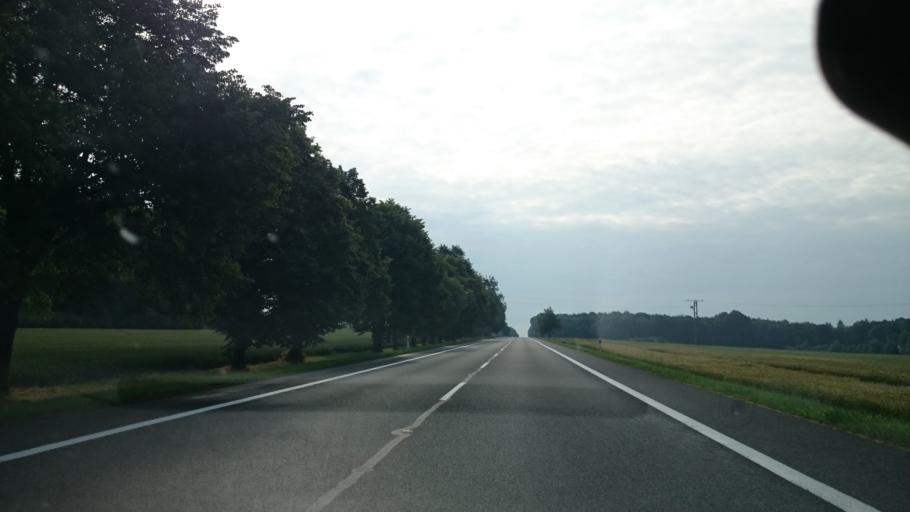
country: PL
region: Opole Voivodeship
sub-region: Powiat strzelecki
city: Jemielnica
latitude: 50.4852
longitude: 18.4248
